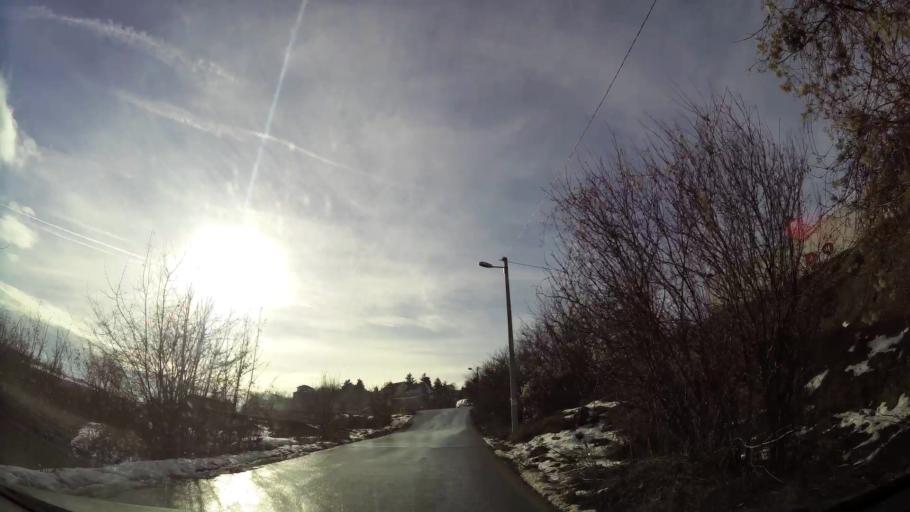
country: RS
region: Central Serbia
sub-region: Belgrade
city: Rakovica
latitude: 44.7207
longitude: 20.4331
